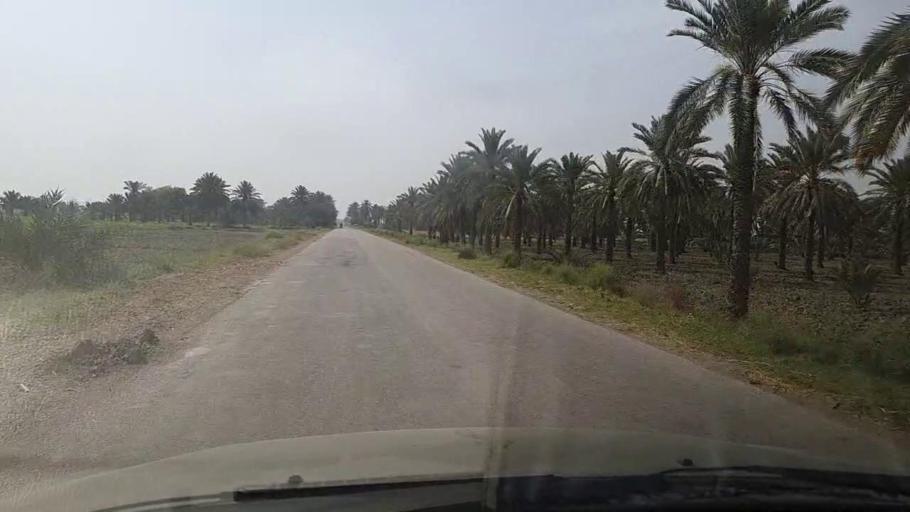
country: PK
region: Sindh
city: Gambat
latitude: 27.4696
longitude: 68.4760
